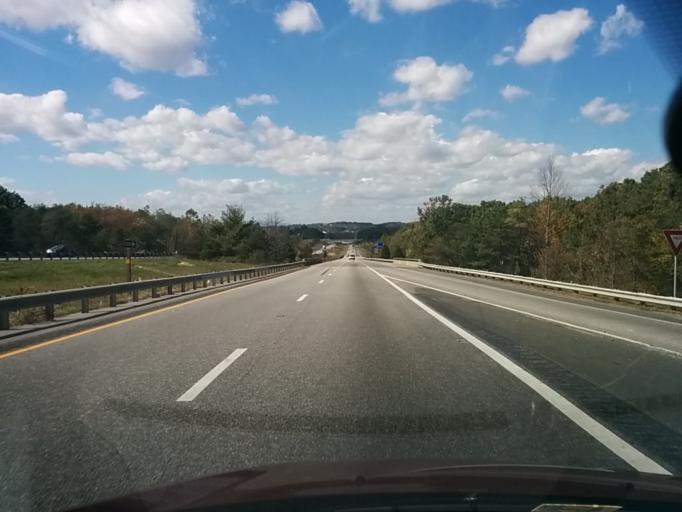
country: US
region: Virginia
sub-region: City of Waynesboro
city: Waynesboro
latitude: 38.0484
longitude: -78.9081
